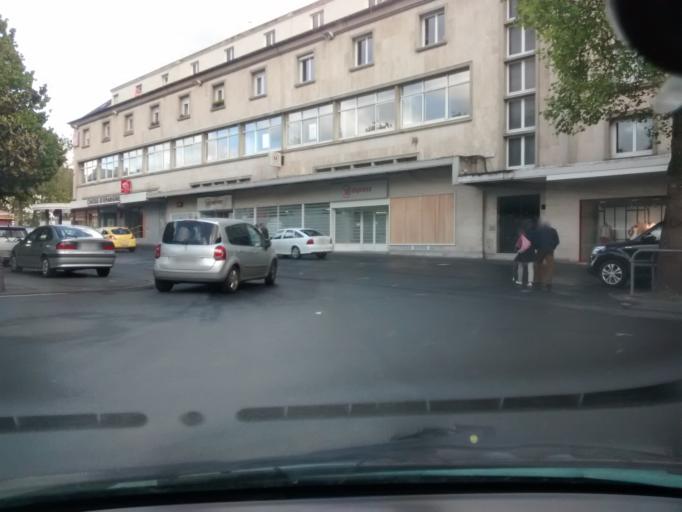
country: FR
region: Lower Normandy
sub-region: Departement de la Manche
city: Saint-Lo
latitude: 49.1155
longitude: -1.0917
